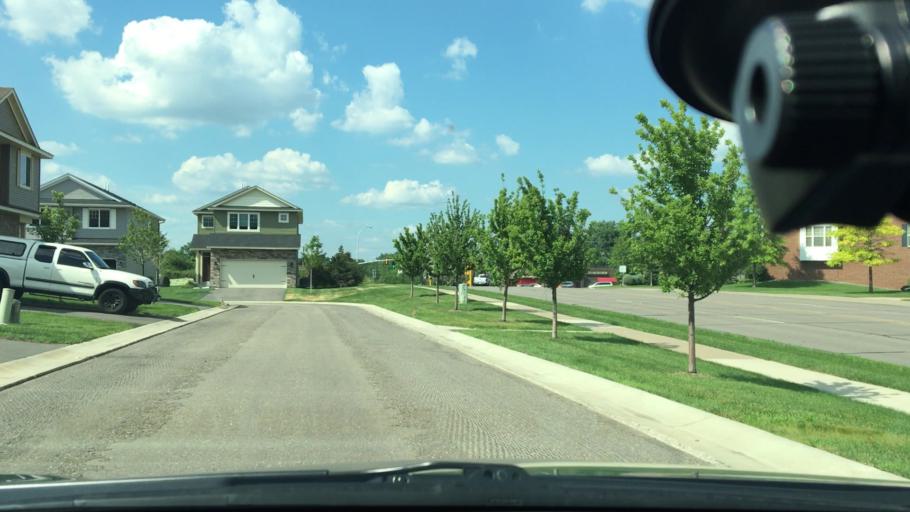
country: US
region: Minnesota
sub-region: Hennepin County
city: New Hope
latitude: 45.0535
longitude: -93.3807
